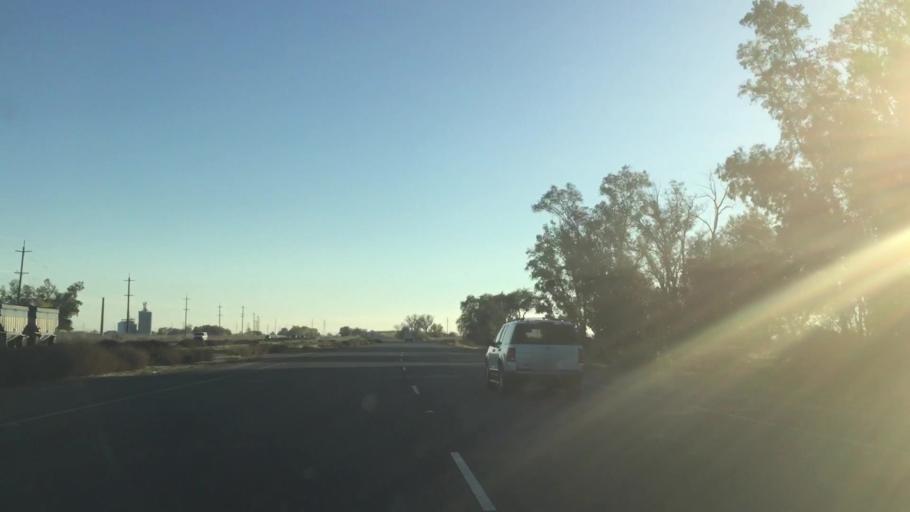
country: US
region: California
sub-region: Yuba County
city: Plumas Lake
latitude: 38.8627
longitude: -121.5436
